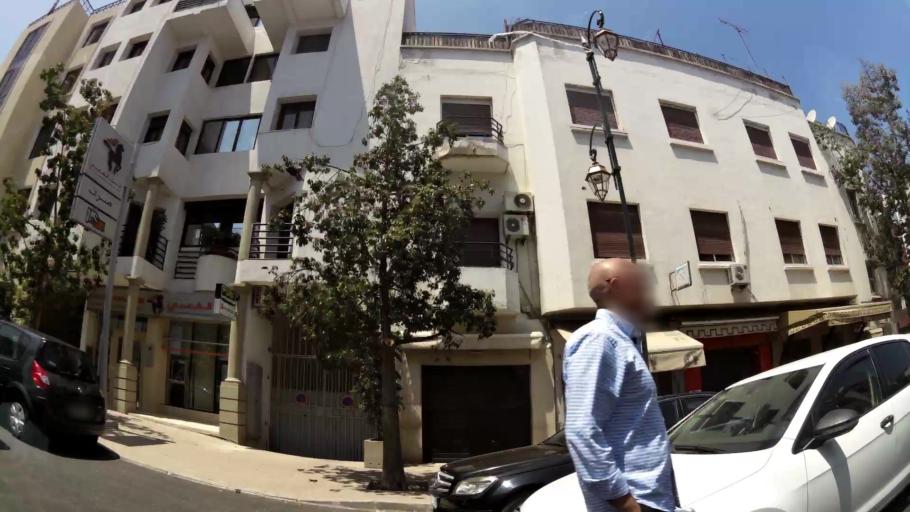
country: MA
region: Rabat-Sale-Zemmour-Zaer
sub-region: Rabat
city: Rabat
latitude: 34.0123
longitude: -6.8287
